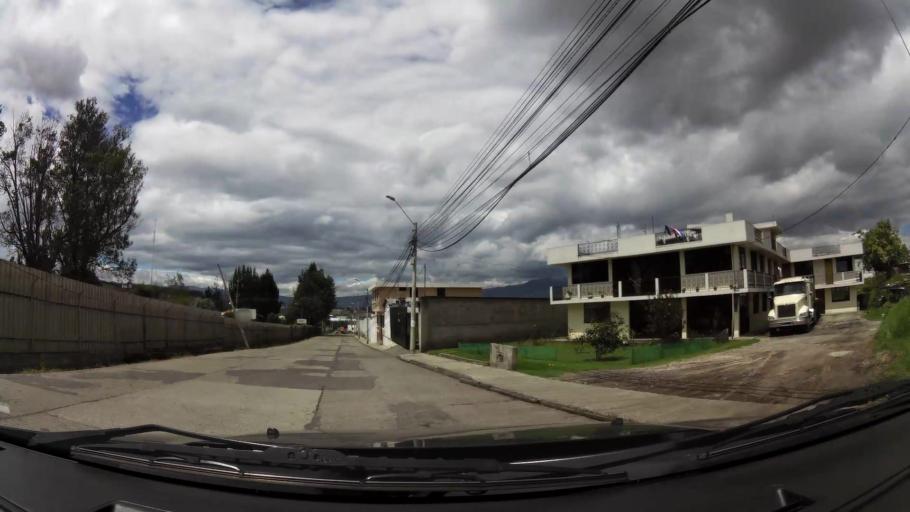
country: EC
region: Pichincha
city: Sangolqui
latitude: -0.3459
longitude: -78.5467
